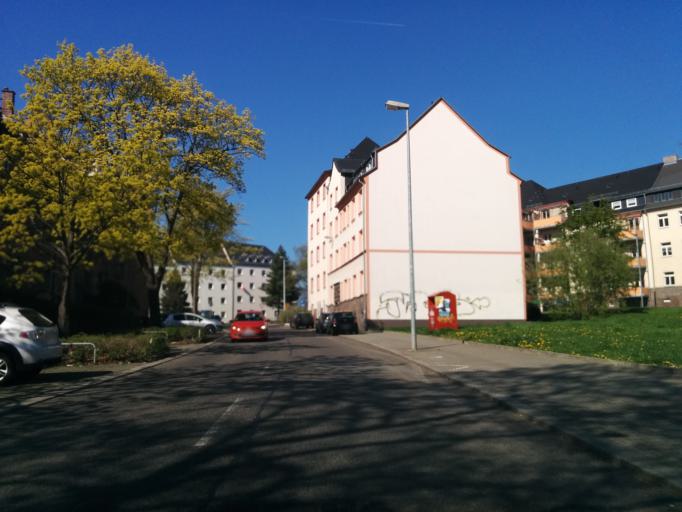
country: DE
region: Saxony
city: Chemnitz
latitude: 50.8204
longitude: 12.9421
